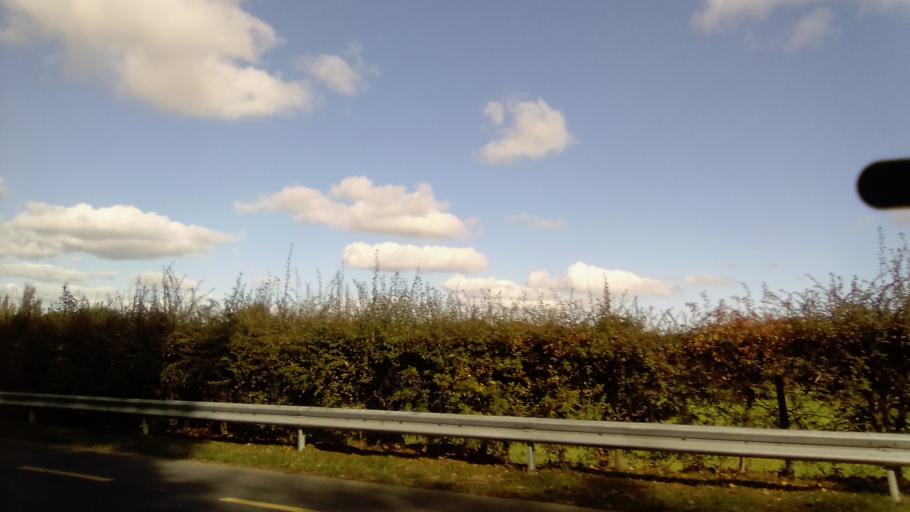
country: IE
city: Kentstown
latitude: 53.6207
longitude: -6.4850
